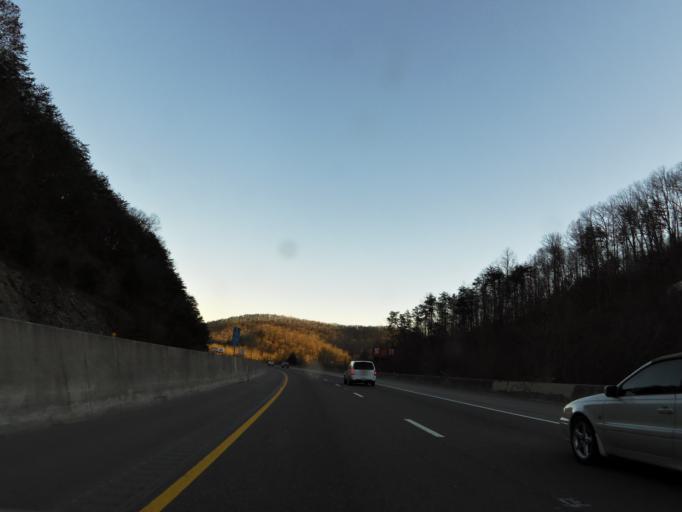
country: US
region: Tennessee
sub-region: Anderson County
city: Norris
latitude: 36.0987
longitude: -84.0207
